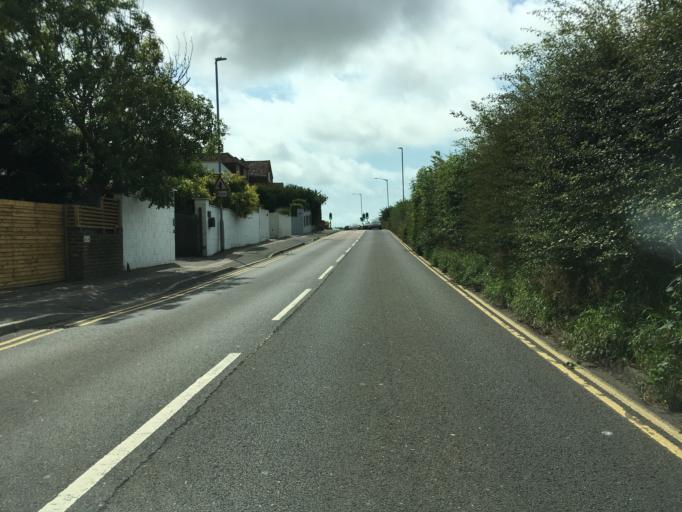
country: GB
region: England
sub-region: Brighton and Hove
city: Rottingdean
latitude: 50.8294
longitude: -0.0729
